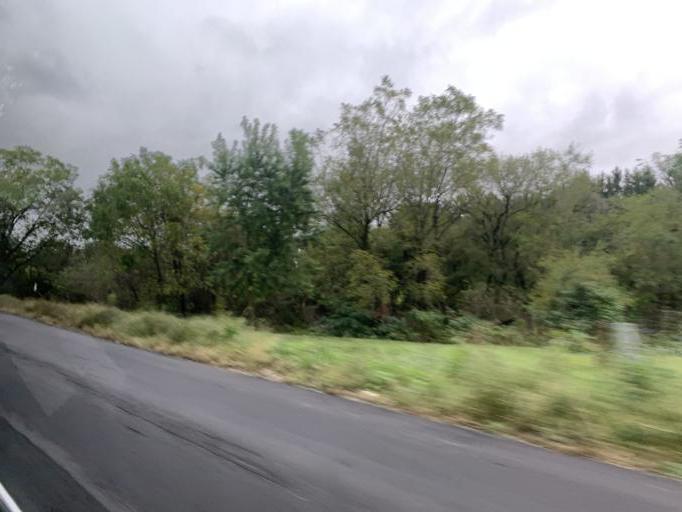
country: US
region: Wisconsin
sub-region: Grant County
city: Muscoda
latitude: 43.2052
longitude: -90.3962
